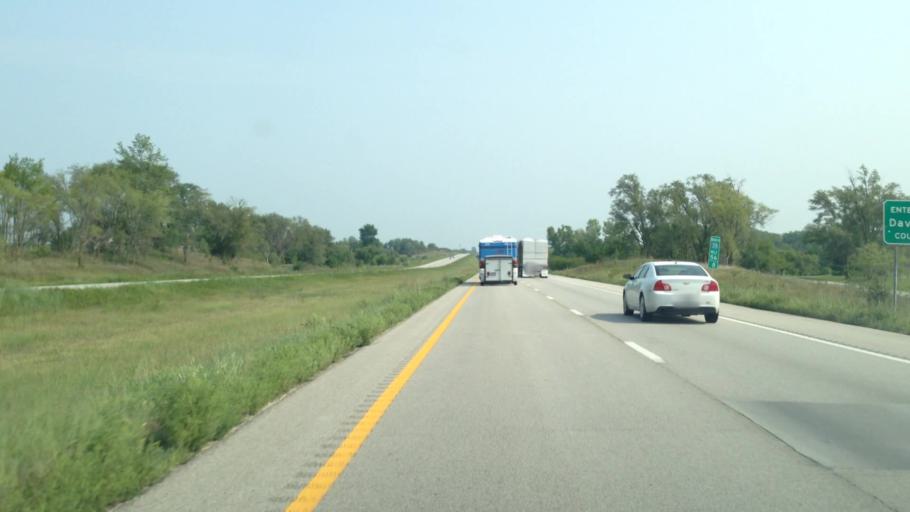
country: US
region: Missouri
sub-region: Clinton County
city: Cameron
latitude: 39.7892
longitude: -94.2052
